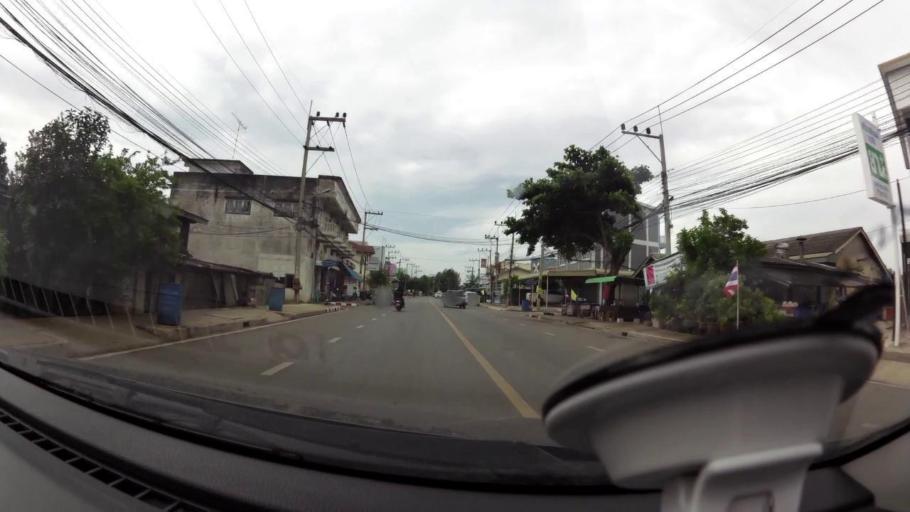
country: TH
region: Prachuap Khiri Khan
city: Pran Buri
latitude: 12.3923
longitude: 99.9872
